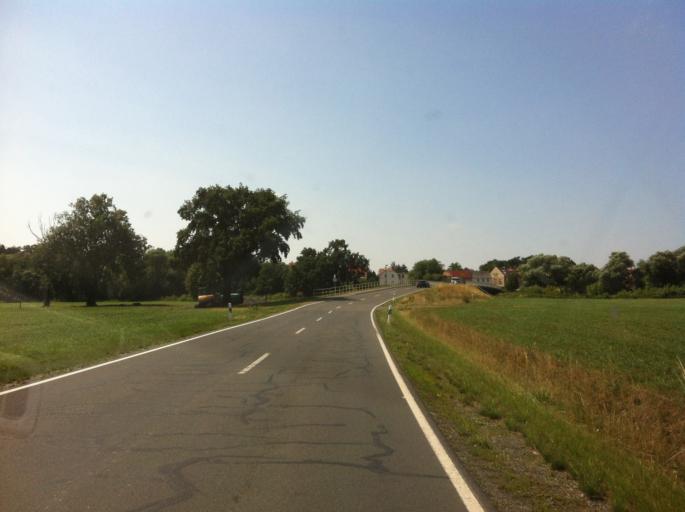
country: DE
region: Saxony
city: Trebsen
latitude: 51.2893
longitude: 12.7629
